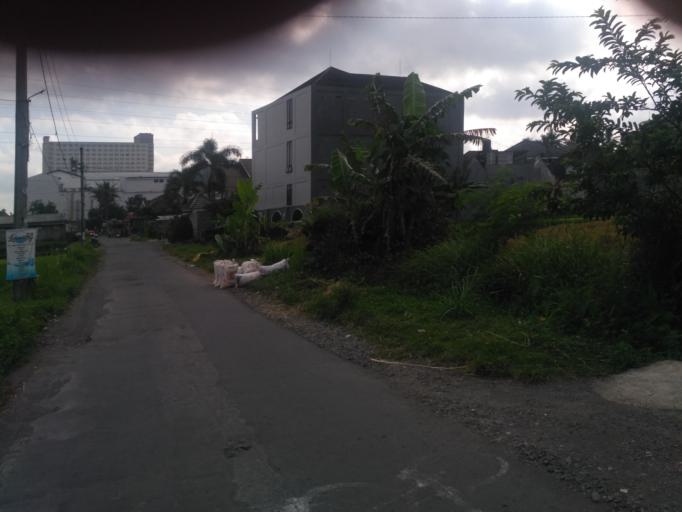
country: ID
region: Daerah Istimewa Yogyakarta
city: Melati
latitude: -7.7574
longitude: 110.3594
